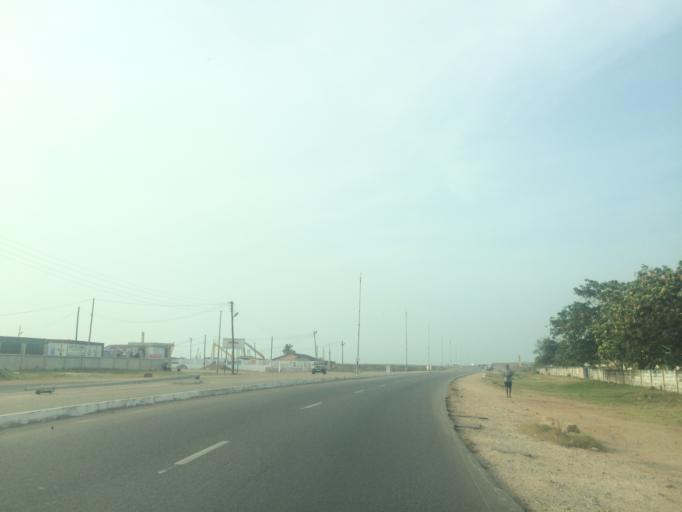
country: GH
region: Greater Accra
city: Accra
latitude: 5.5357
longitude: -0.2214
